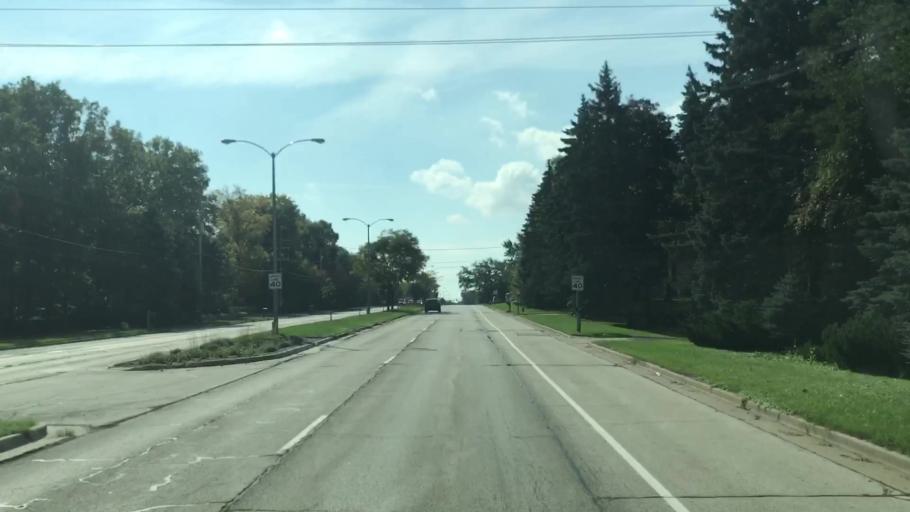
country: US
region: Wisconsin
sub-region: Waukesha County
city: Butler
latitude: 43.1551
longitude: -88.0449
